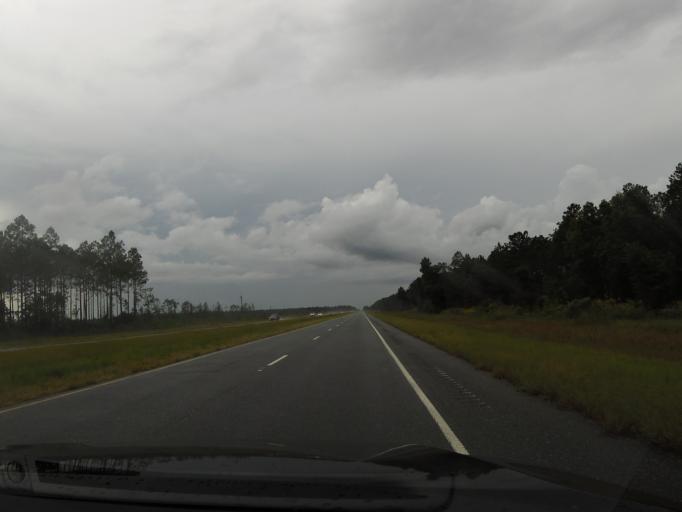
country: US
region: Georgia
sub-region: Wayne County
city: Jesup
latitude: 31.4990
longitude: -81.7534
